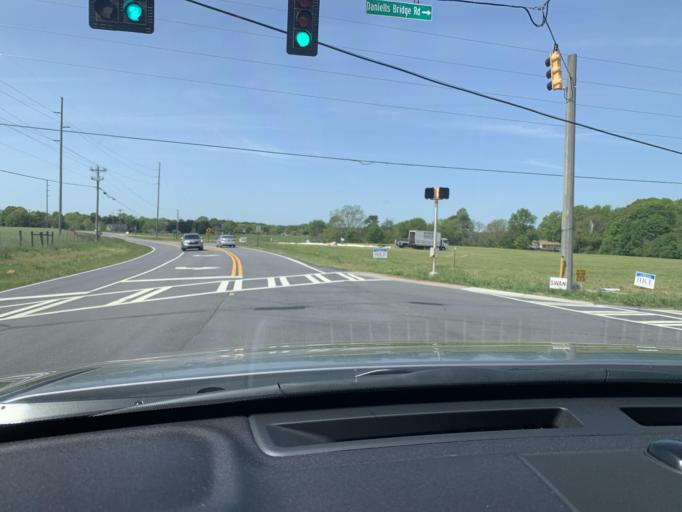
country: US
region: Georgia
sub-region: Oconee County
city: Watkinsville
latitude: 33.8871
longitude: -83.4279
